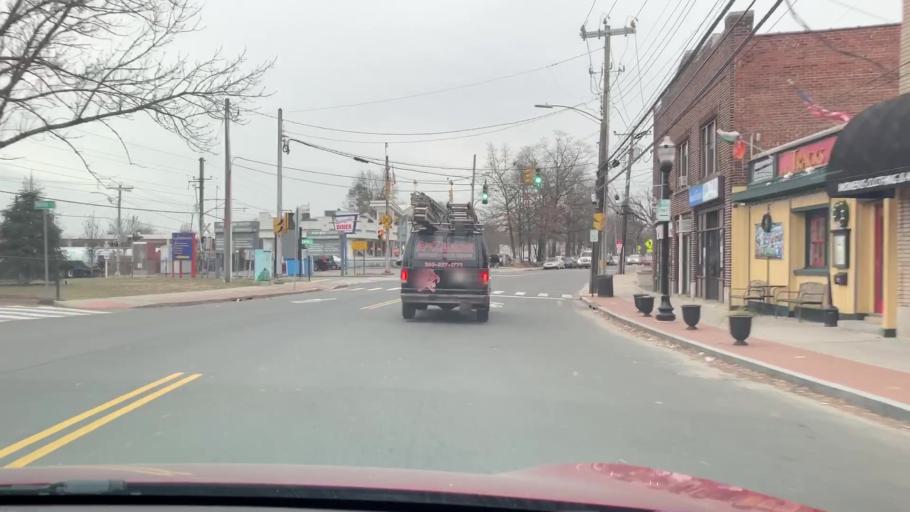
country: US
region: Connecticut
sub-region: Fairfield County
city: Stamford
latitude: 41.0903
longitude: -73.5177
